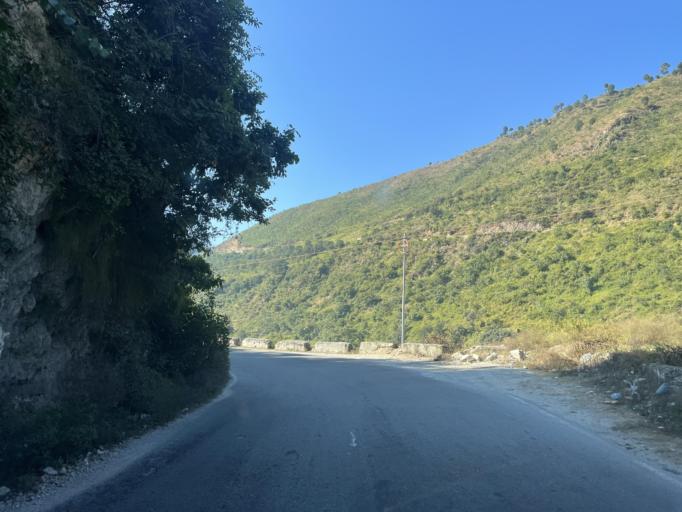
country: IN
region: Uttarakhand
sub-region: Naini Tal
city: Naini Tal
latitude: 29.5179
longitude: 79.4802
